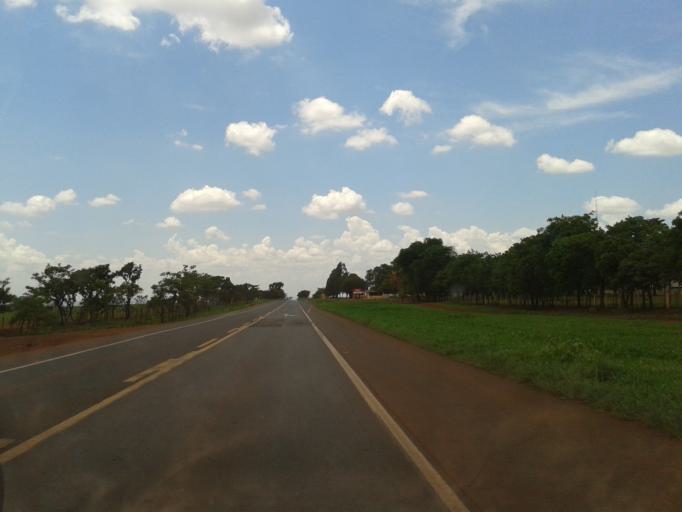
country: BR
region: Goias
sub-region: Goiatuba
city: Goiatuba
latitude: -18.2476
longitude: -49.6944
